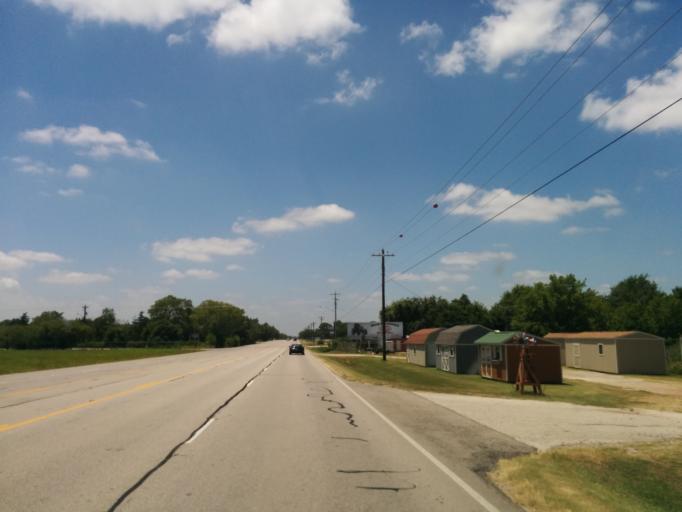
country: US
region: Texas
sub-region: Brazos County
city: Bryan
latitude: 30.7190
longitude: -96.3390
